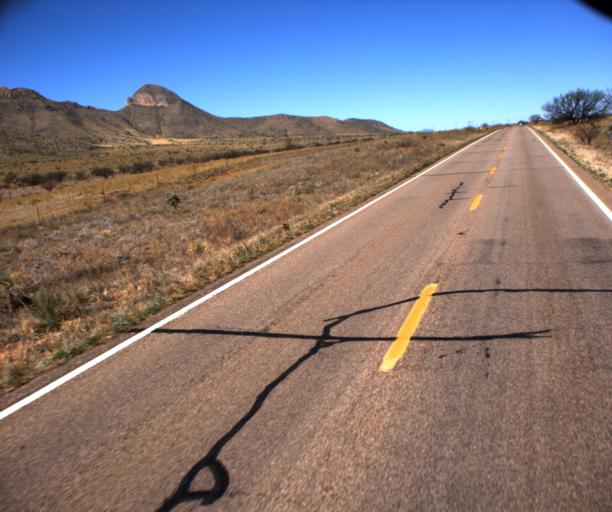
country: US
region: Arizona
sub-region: Cochise County
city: Huachuca City
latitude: 31.7147
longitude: -110.4633
